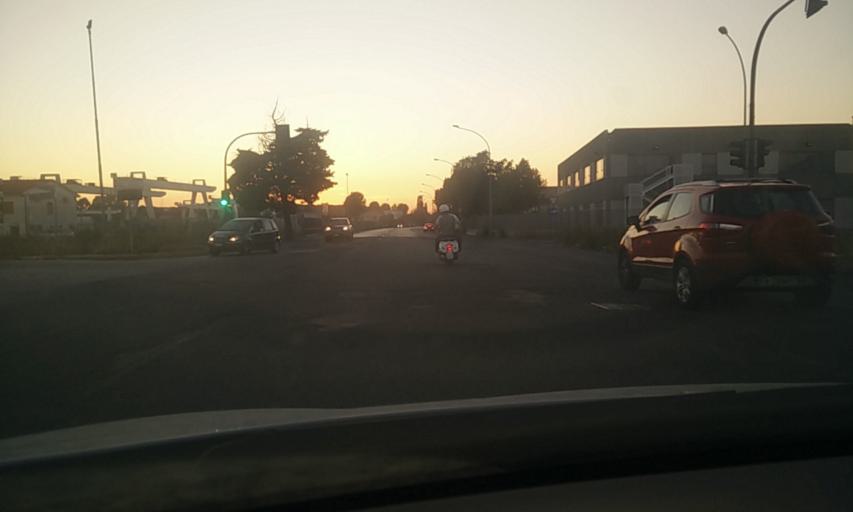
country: IT
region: Tuscany
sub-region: Provincia di Massa-Carrara
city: Carrara
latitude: 44.0330
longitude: 10.0866
